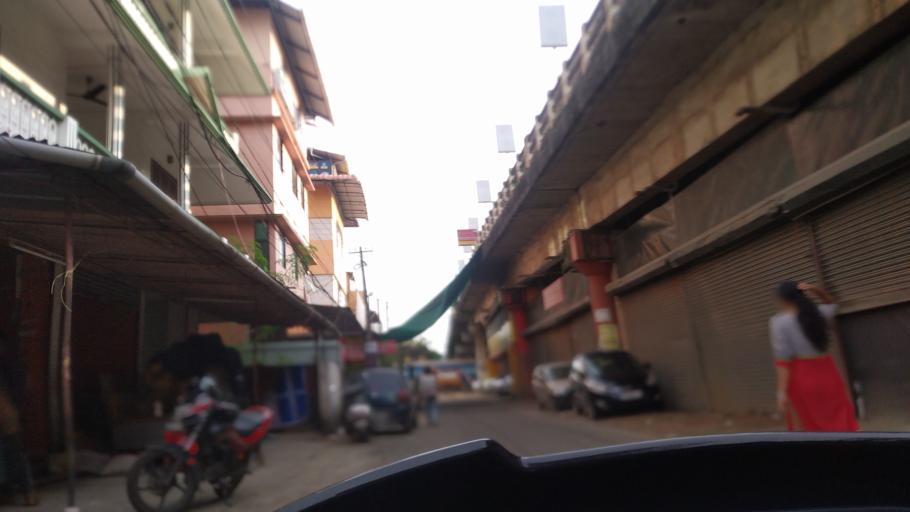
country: IN
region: Kerala
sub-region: Ernakulam
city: Cochin
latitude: 9.9817
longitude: 76.2960
